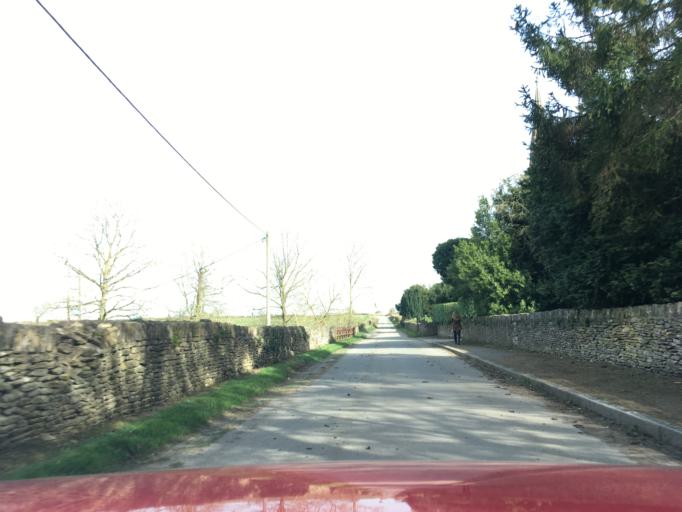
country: GB
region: England
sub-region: Wiltshire
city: Luckington
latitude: 51.5465
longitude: -2.2305
